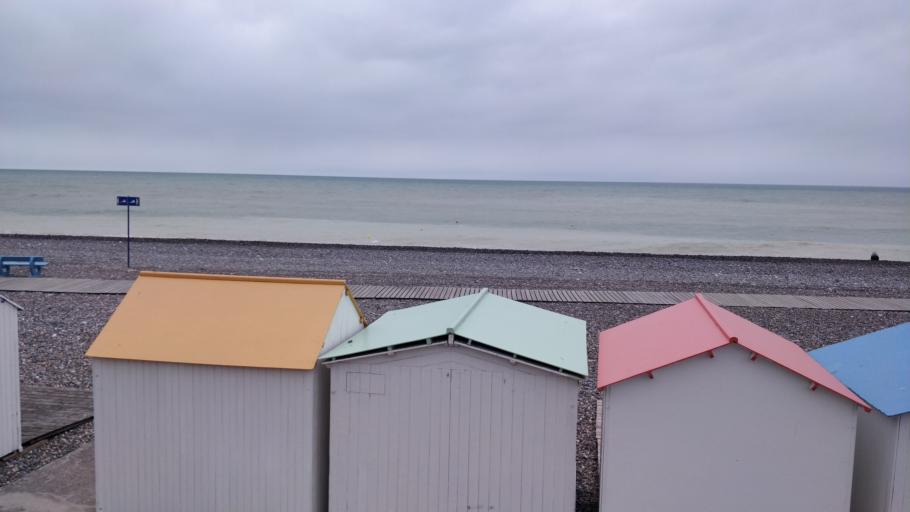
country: FR
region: Haute-Normandie
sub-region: Departement de la Seine-Maritime
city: Le Treport
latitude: 50.0616
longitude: 1.3667
